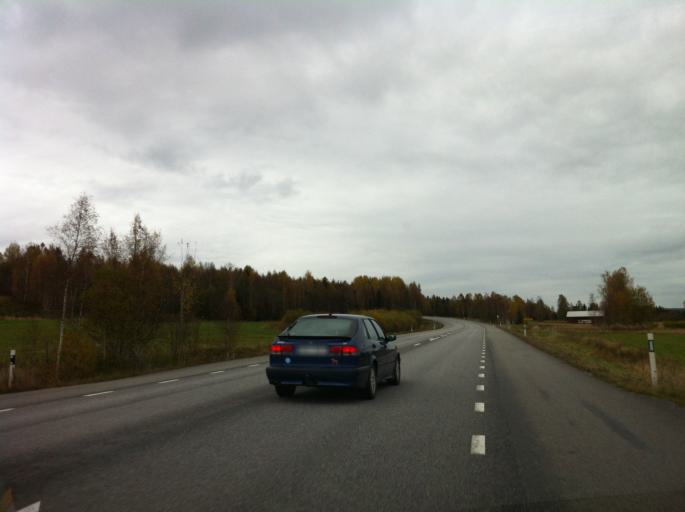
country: SE
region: OErebro
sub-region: Lindesbergs Kommun
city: Stora
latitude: 59.7318
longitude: 15.1360
